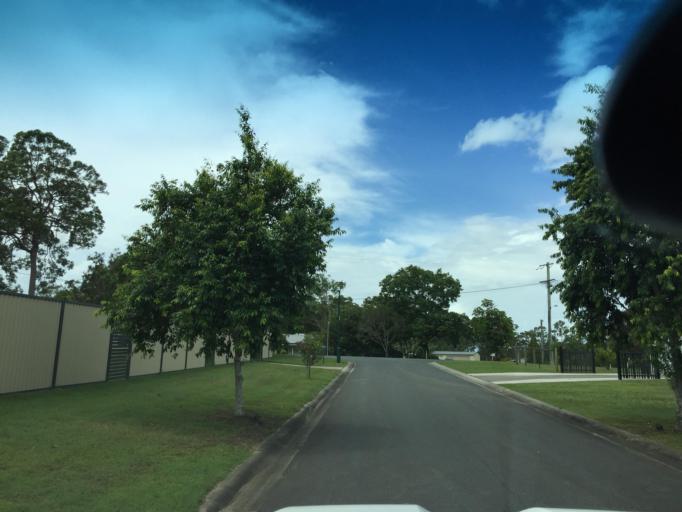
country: AU
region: Queensland
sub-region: Moreton Bay
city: Morayfield
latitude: -27.1179
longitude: 152.9040
